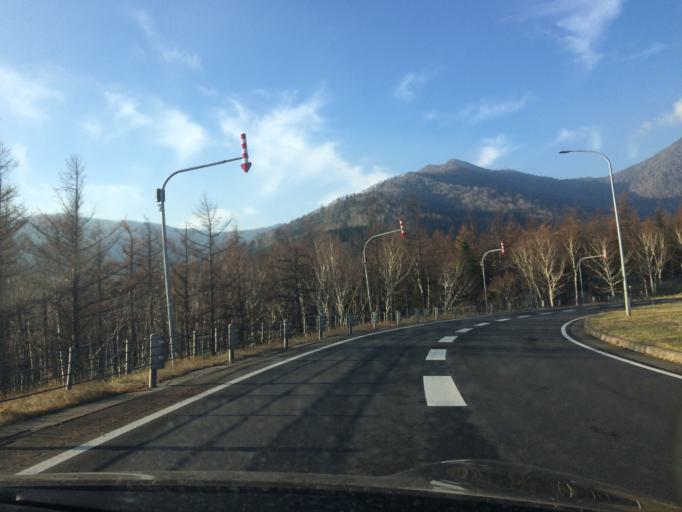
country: JP
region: Hokkaido
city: Otofuke
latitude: 42.9571
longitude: 142.7947
